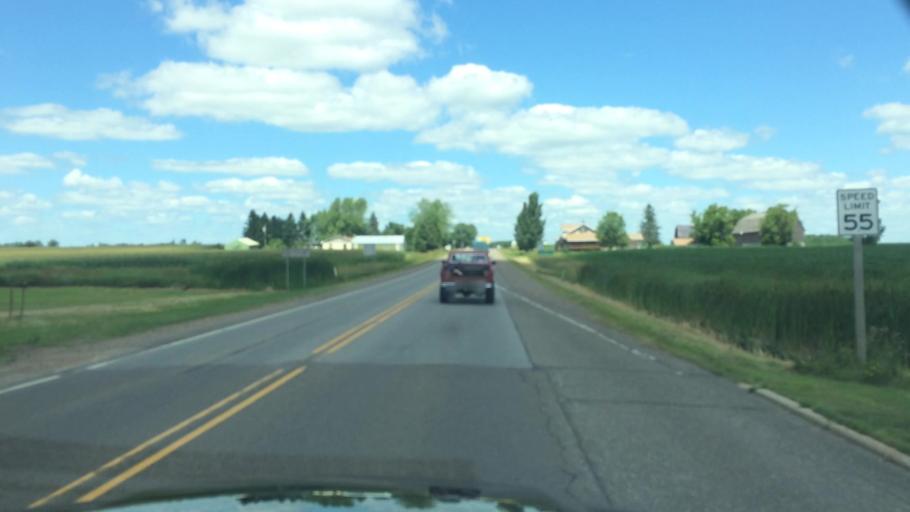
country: US
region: Wisconsin
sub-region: Taylor County
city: Medford
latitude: 45.0809
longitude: -90.3147
